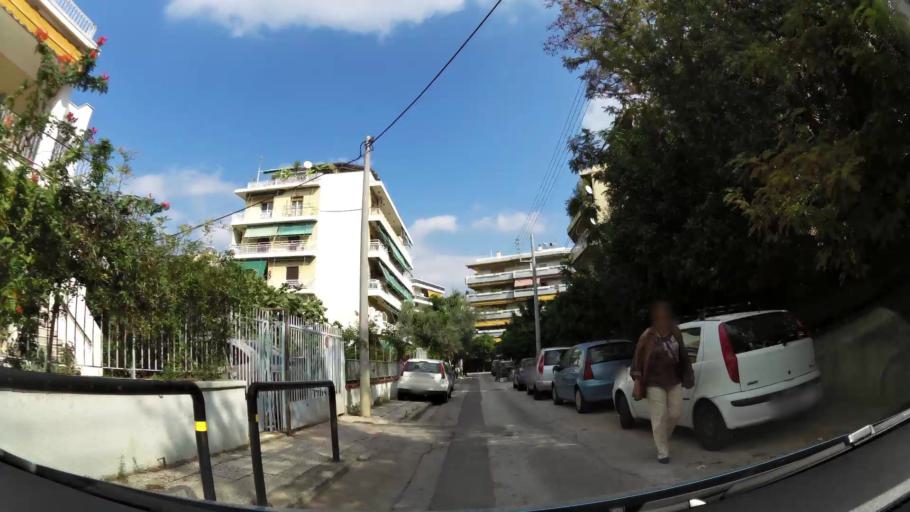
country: GR
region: Attica
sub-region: Nomarchia Athinas
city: Cholargos
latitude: 38.0043
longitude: 23.7982
